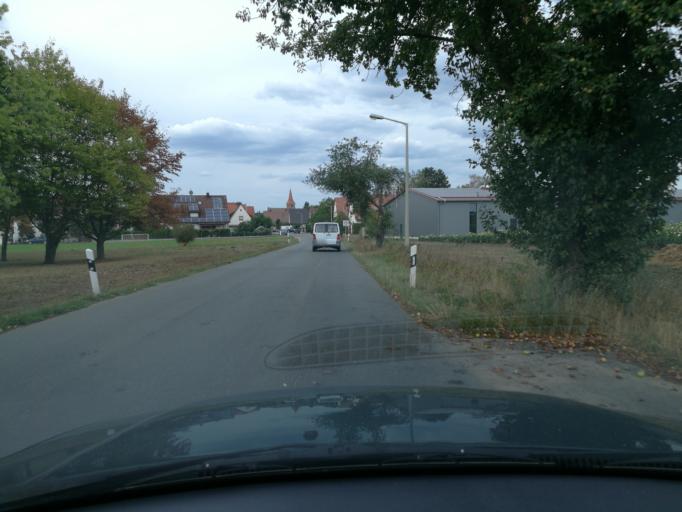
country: DE
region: Bavaria
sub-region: Regierungsbezirk Mittelfranken
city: Wetzendorf
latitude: 49.5075
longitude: 11.0475
